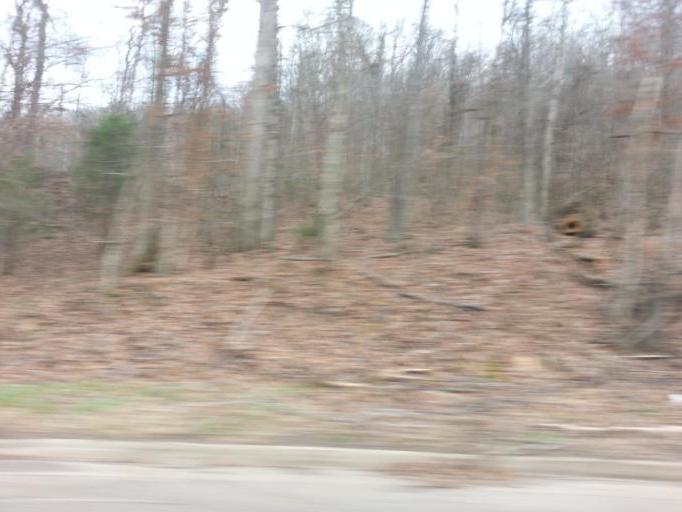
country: US
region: Tennessee
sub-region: Hamilton County
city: Sale Creek
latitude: 35.4062
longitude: -85.1018
